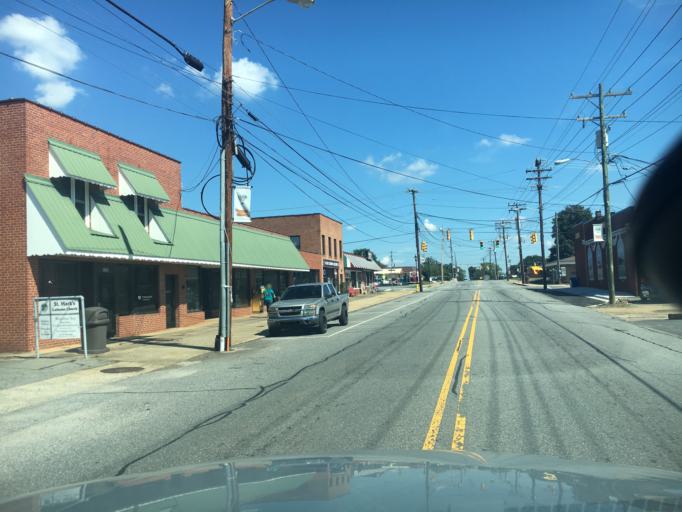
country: US
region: North Carolina
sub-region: Catawba County
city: Claremont
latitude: 35.7150
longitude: -81.1480
